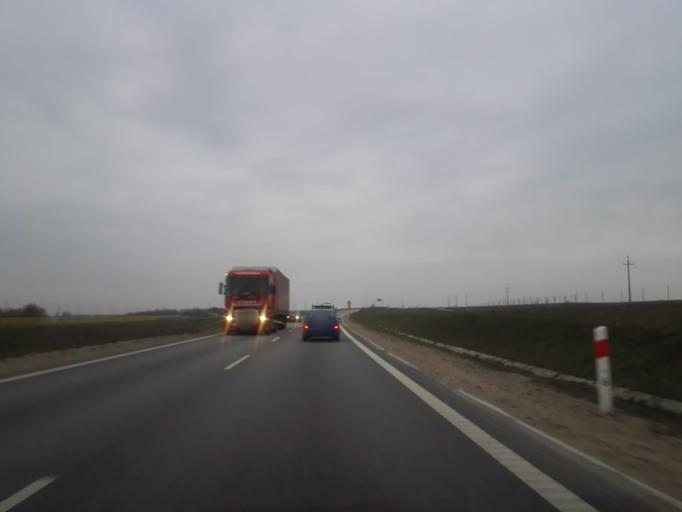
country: PL
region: Podlasie
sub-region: Powiat kolnenski
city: Stawiski
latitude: 53.3980
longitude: 22.1555
